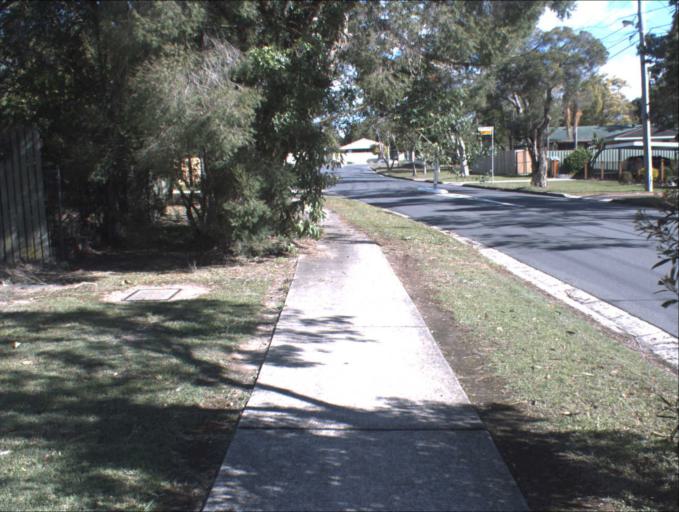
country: AU
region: Queensland
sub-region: Logan
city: Waterford West
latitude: -27.6806
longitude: 153.1020
